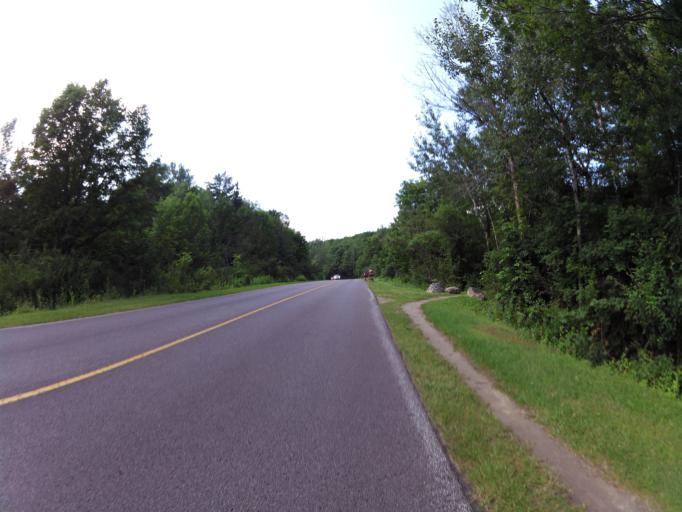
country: CA
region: Quebec
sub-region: Outaouais
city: Gatineau
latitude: 45.4555
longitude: -75.7868
